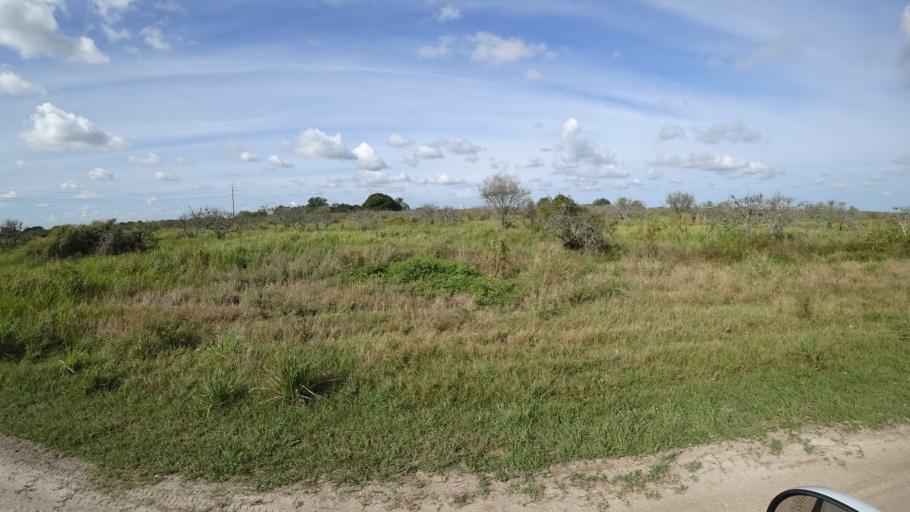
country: US
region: Florida
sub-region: Hillsborough County
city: Wimauma
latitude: 27.6044
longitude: -82.2880
